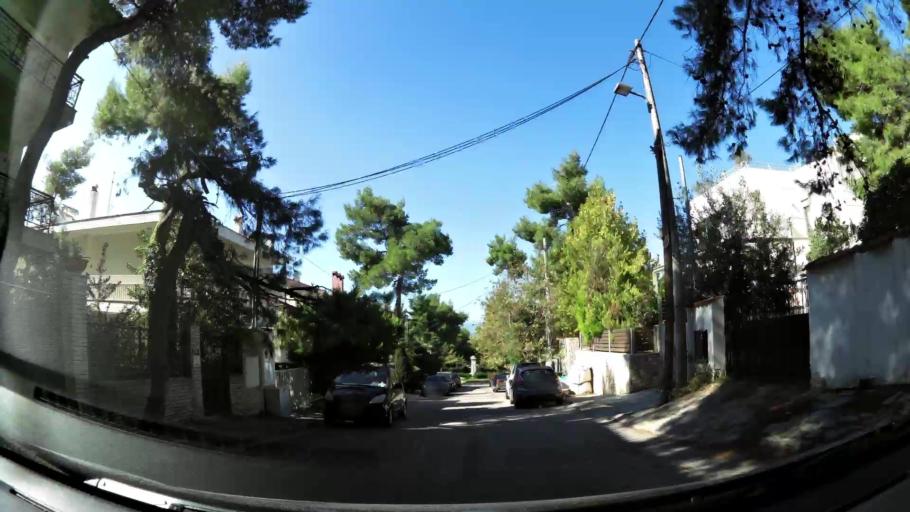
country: GR
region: Attica
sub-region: Nomarchia Anatolikis Attikis
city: Drosia
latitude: 38.1092
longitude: 23.8670
